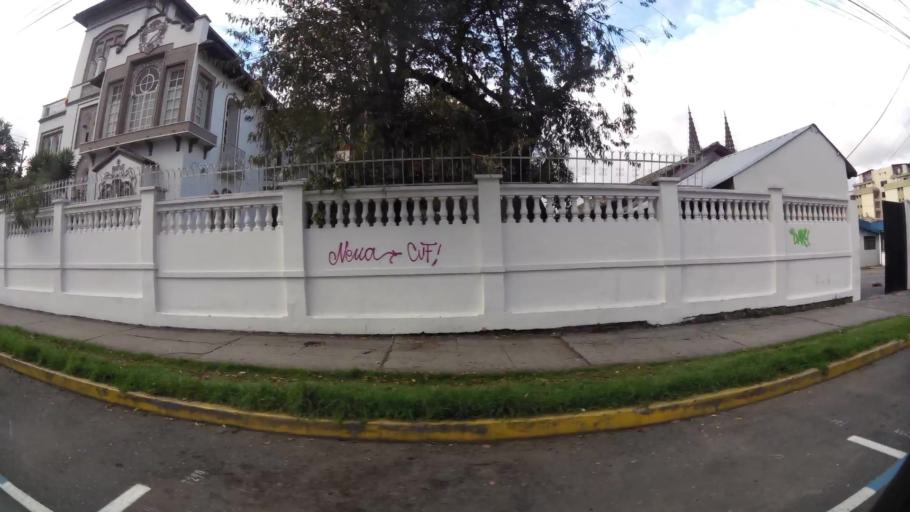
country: EC
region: Pichincha
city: Quito
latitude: -0.2054
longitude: -78.4974
